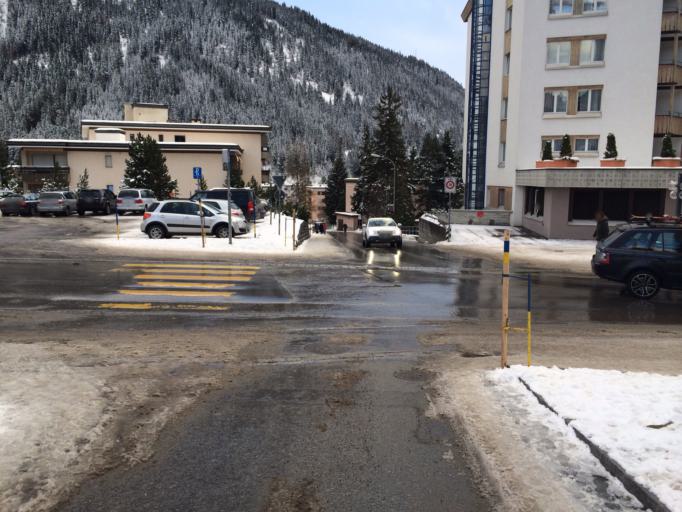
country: CH
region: Grisons
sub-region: Praettigau/Davos District
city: Davos
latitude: 46.8014
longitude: 9.8324
